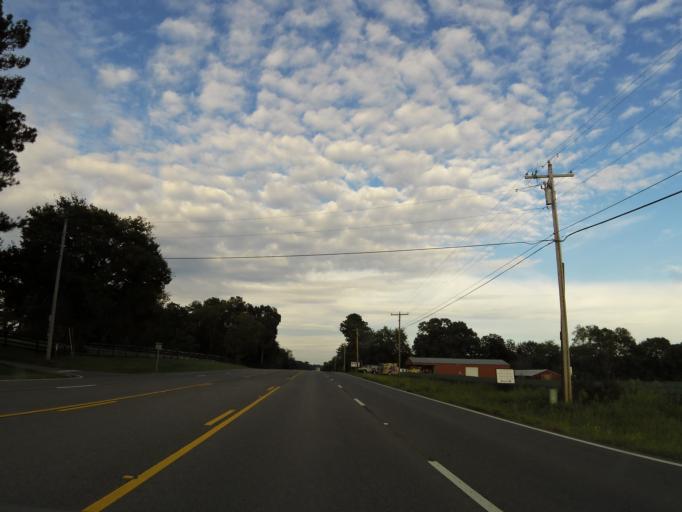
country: US
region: Alabama
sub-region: Lauderdale County
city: Rogersville
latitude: 34.8019
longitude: -87.2077
